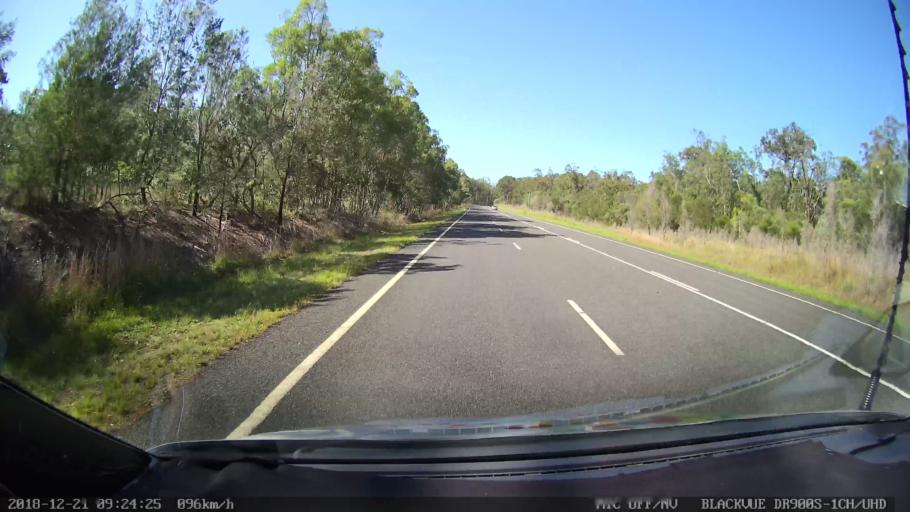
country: AU
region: New South Wales
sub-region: Clarence Valley
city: Maclean
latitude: -29.3672
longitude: 153.0163
